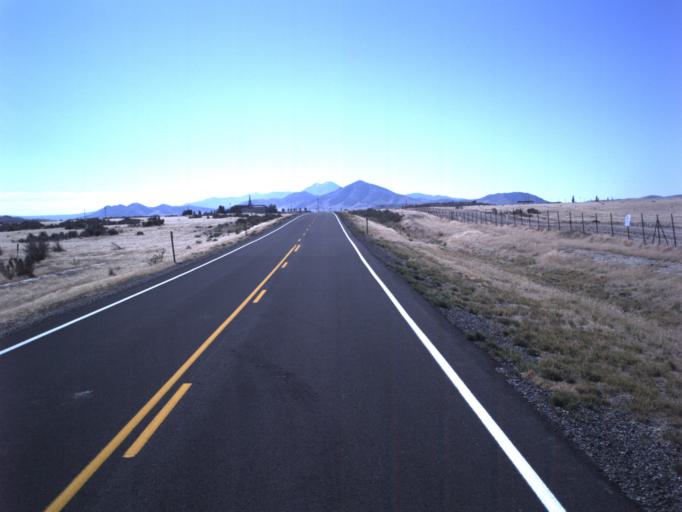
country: US
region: Utah
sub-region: Tooele County
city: Grantsville
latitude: 40.2408
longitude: -112.7232
